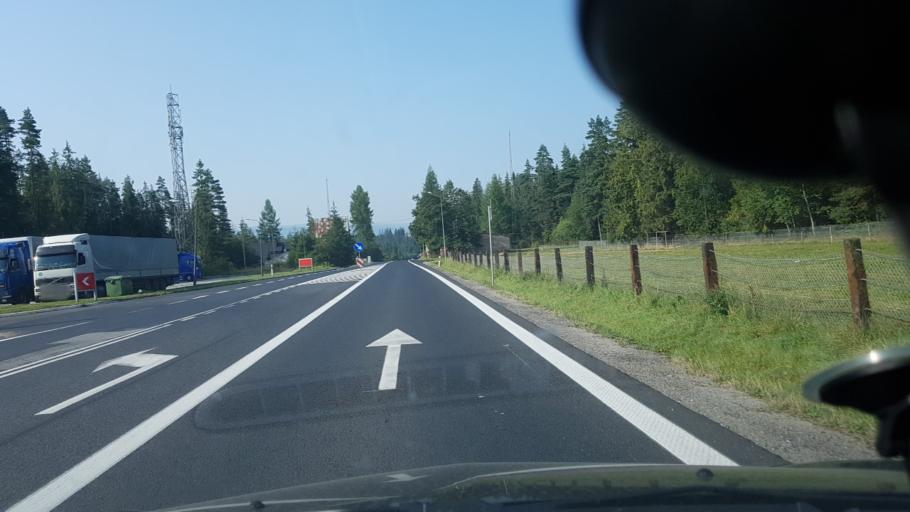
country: PL
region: Lesser Poland Voivodeship
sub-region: Powiat nowotarski
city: Chyzne
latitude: 49.4128
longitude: 19.6633
